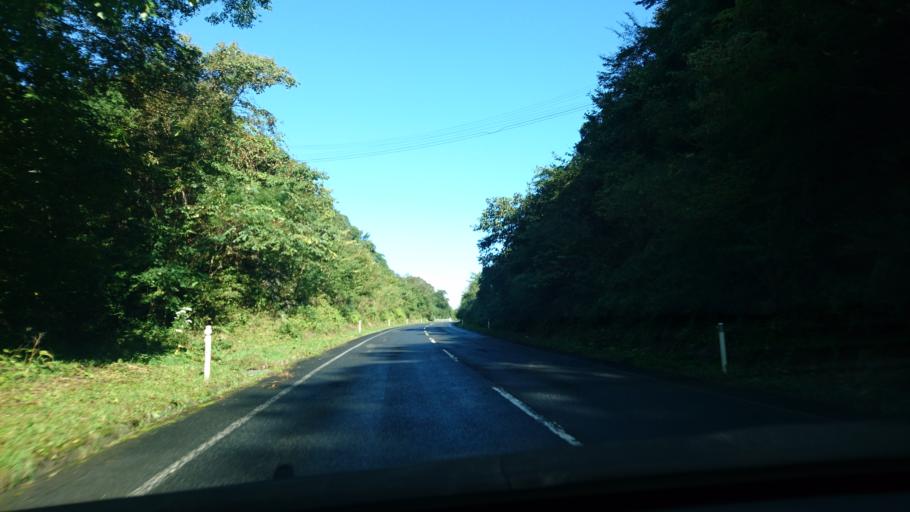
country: JP
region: Iwate
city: Ichinoseki
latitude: 39.0151
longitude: 141.0253
